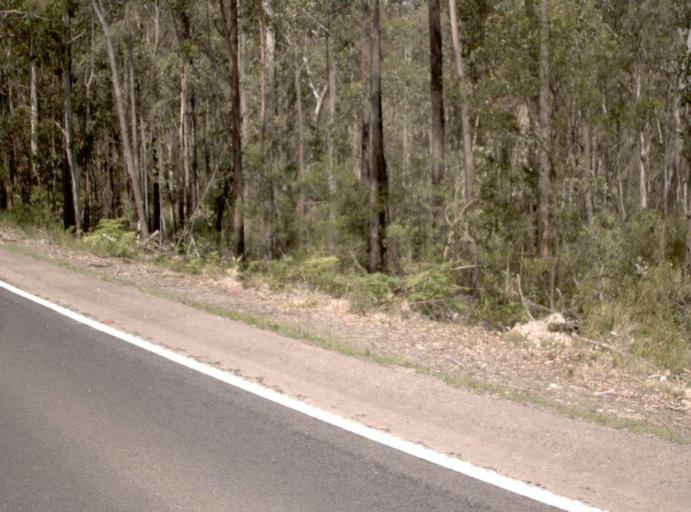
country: AU
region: New South Wales
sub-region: Bombala
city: Bombala
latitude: -37.5656
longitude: 149.1019
